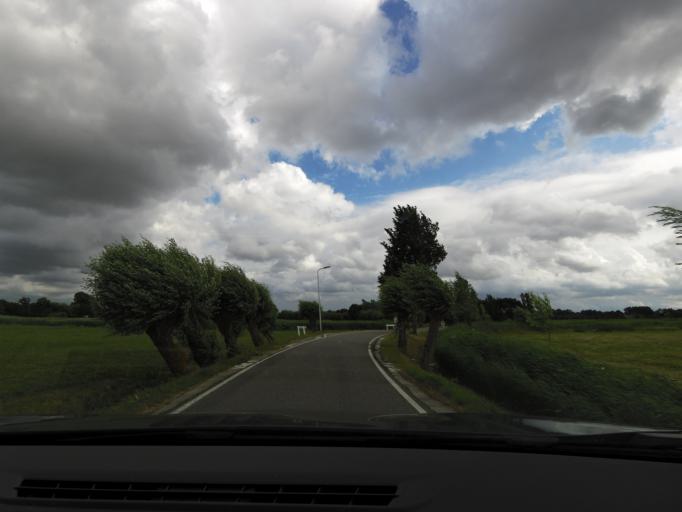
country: NL
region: South Holland
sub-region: Gemeente Vlaardingen
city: Vlaardingen
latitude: 51.9488
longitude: 4.3385
